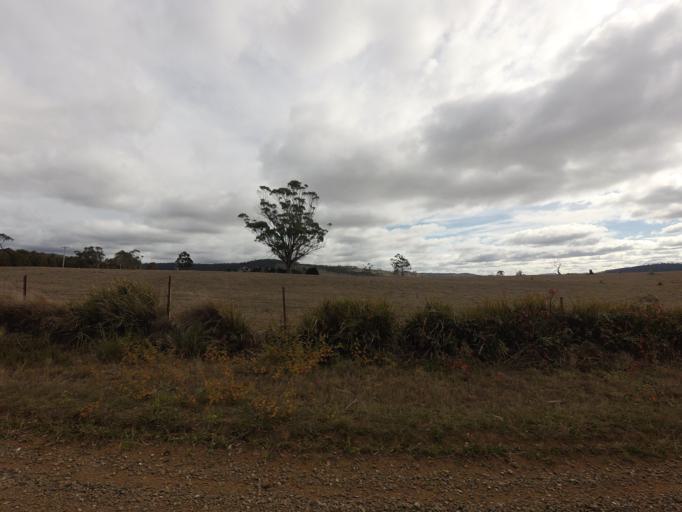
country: AU
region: Tasmania
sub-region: Brighton
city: Bridgewater
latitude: -42.4391
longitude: 147.3858
